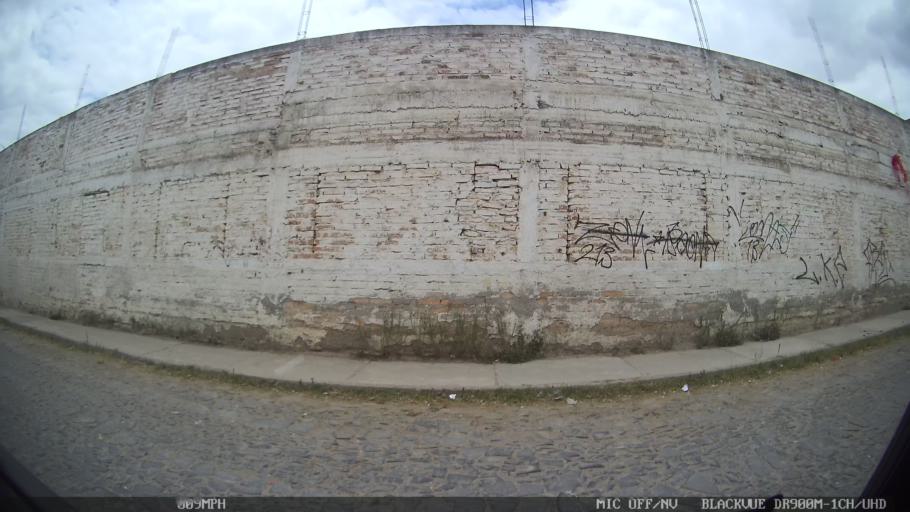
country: MX
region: Jalisco
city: Tonala
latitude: 20.6513
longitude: -103.2557
